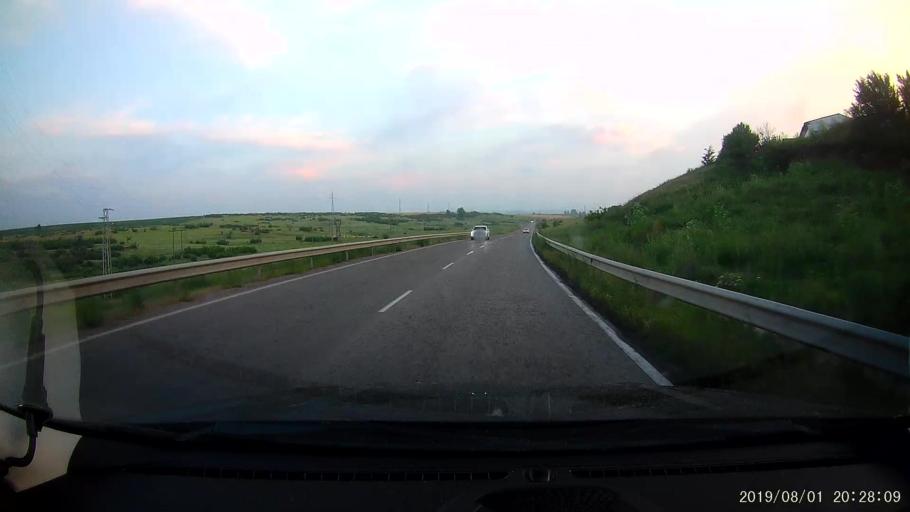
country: BG
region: Yambol
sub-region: Obshtina Elkhovo
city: Elkhovo
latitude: 42.1714
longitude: 26.5808
